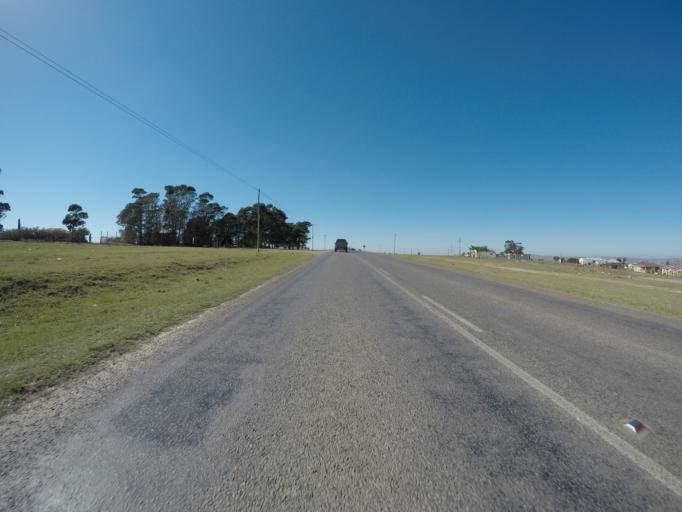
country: ZA
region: Eastern Cape
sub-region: OR Tambo District Municipality
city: Mthatha
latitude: -31.7900
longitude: 28.7445
